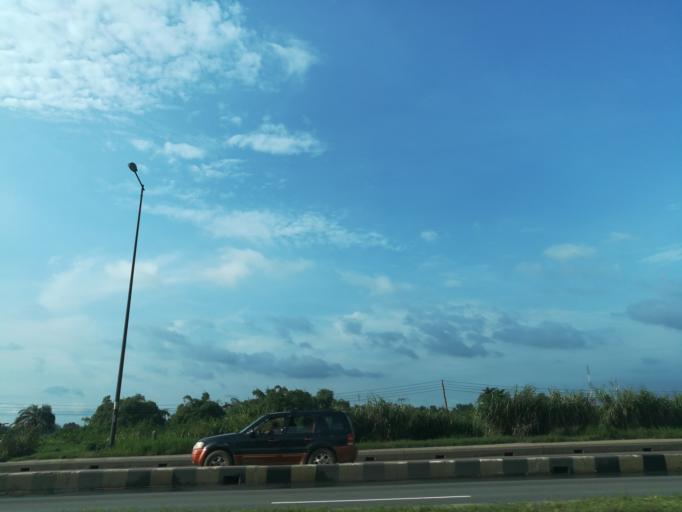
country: NG
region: Lagos
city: Ebute Ikorodu
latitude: 6.6088
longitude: 3.4371
